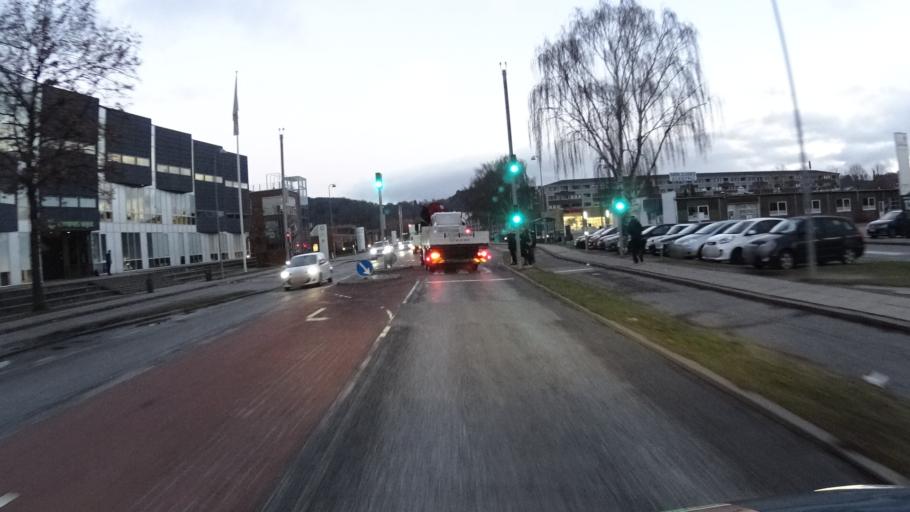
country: DK
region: South Denmark
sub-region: Vejle Kommune
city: Vejle
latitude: 55.7101
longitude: 9.5228
